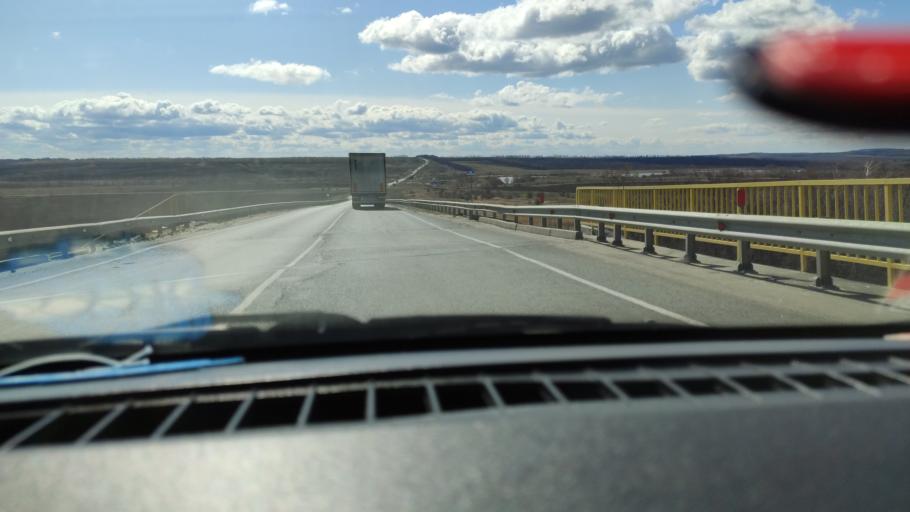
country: RU
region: Saratov
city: Dukhovnitskoye
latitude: 52.7473
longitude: 48.2507
